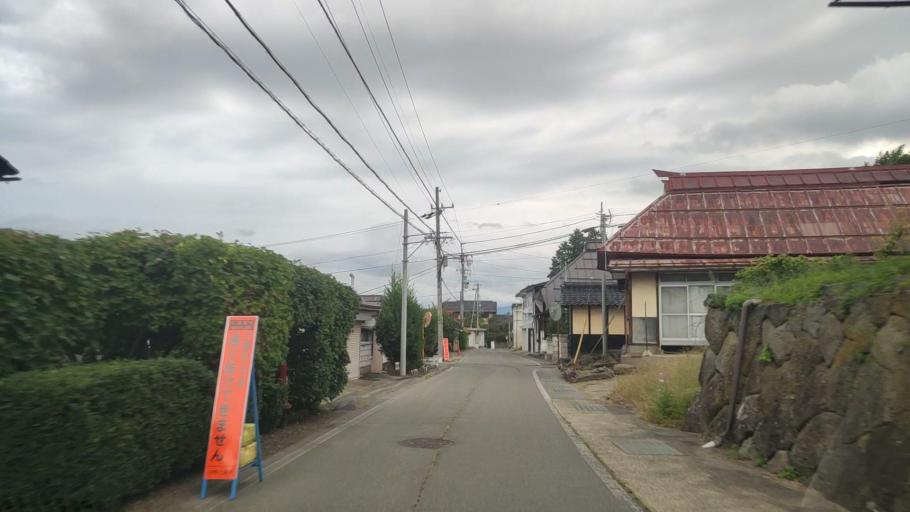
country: JP
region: Nagano
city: Nakano
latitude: 36.7868
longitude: 138.3663
